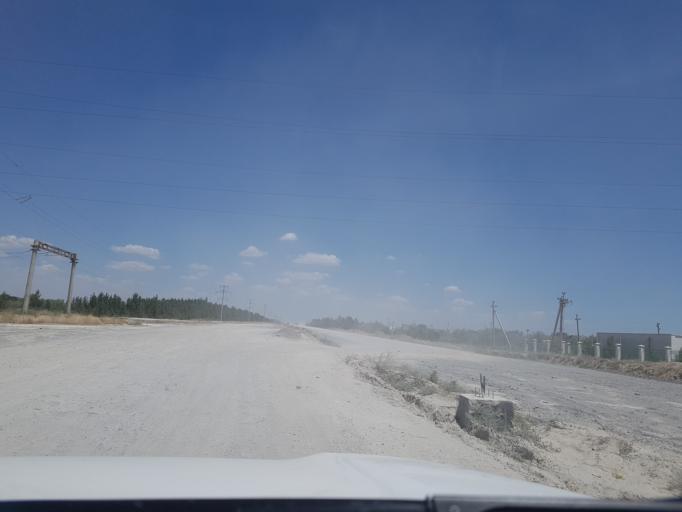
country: TM
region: Ahal
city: Abadan
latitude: 38.1738
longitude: 57.9486
